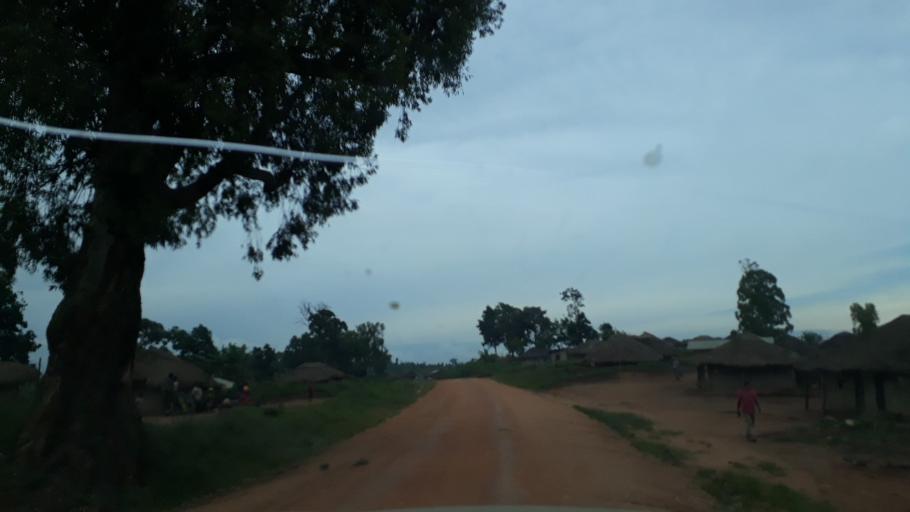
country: UG
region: Northern Region
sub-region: Zombo District
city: Paidha
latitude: 2.0590
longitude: 30.6339
